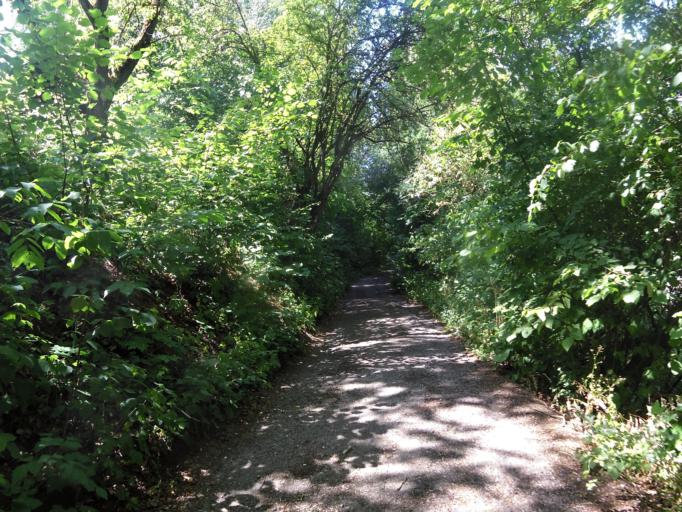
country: DE
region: Bavaria
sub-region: Regierungsbezirk Unterfranken
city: Wuerzburg
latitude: 49.8131
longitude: 9.9594
